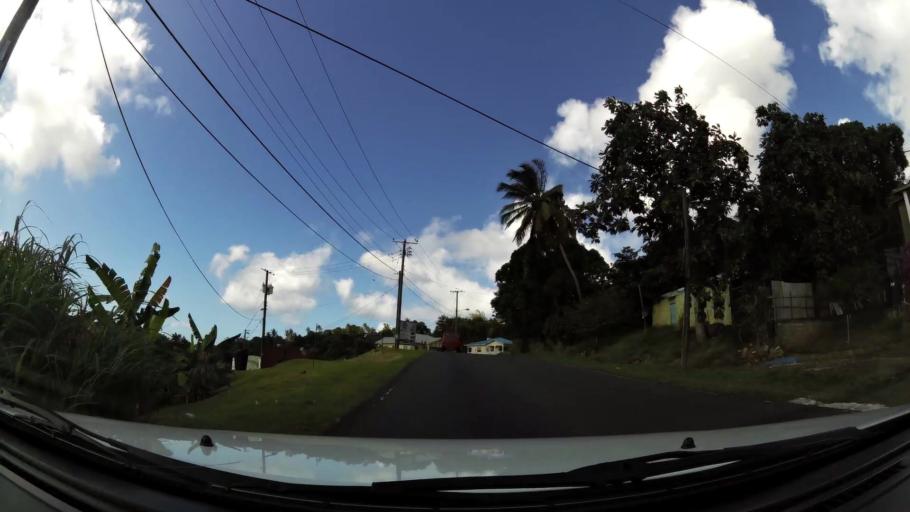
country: LC
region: Castries Quarter
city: Castries
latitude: 13.9960
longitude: -60.9990
